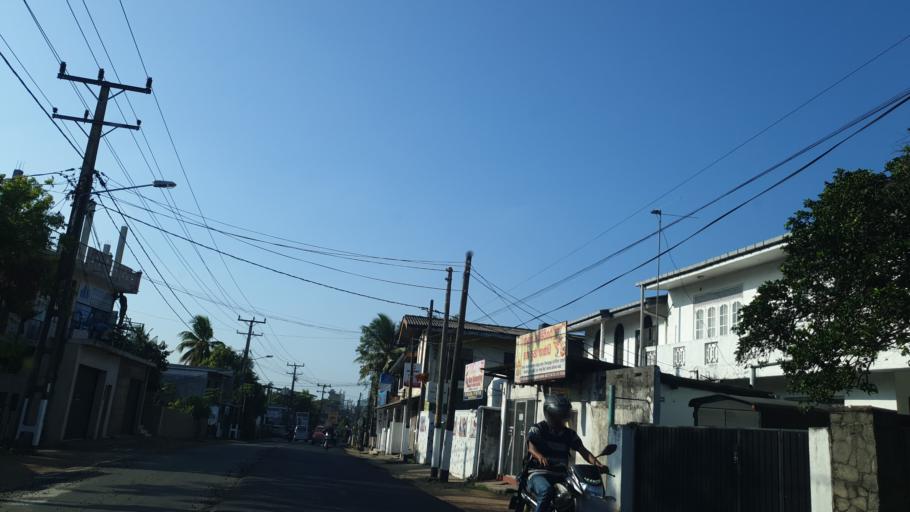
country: LK
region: Western
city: Sri Jayewardenepura Kotte
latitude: 6.8685
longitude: 79.9088
